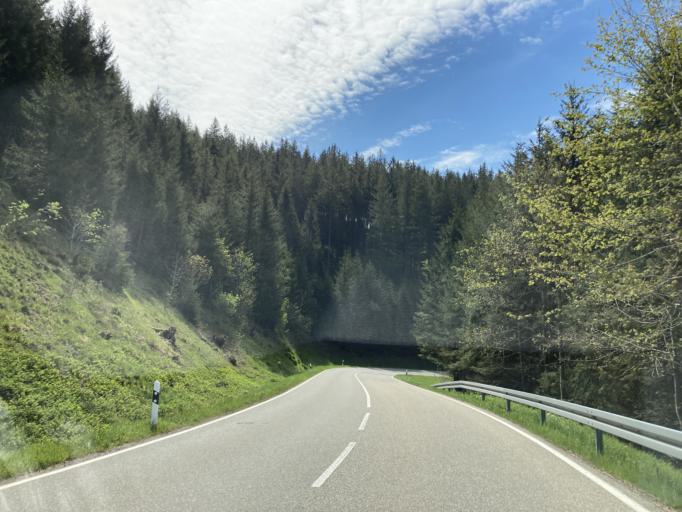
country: DE
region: Baden-Wuerttemberg
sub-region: Freiburg Region
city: Schonwald im Schwarzwald
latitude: 48.0804
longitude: 8.2103
